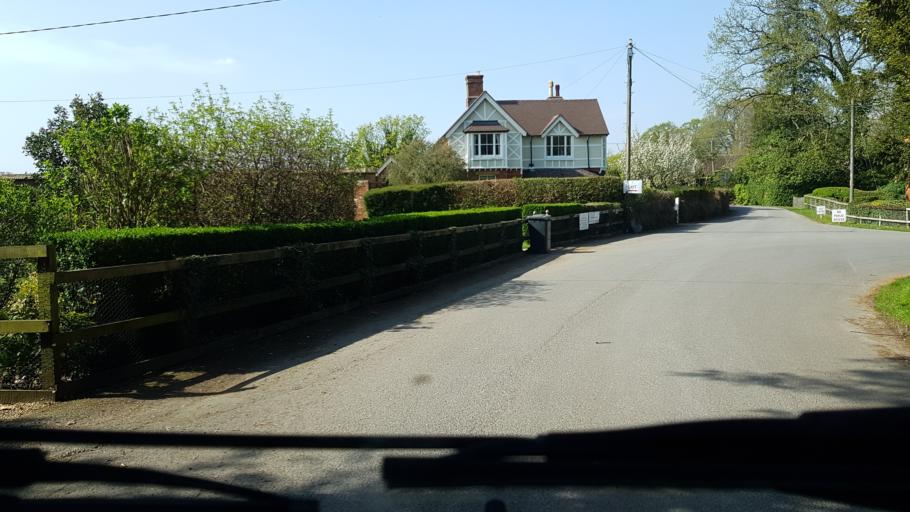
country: GB
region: England
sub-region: Hampshire
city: Highclere
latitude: 51.3301
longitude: -1.3615
